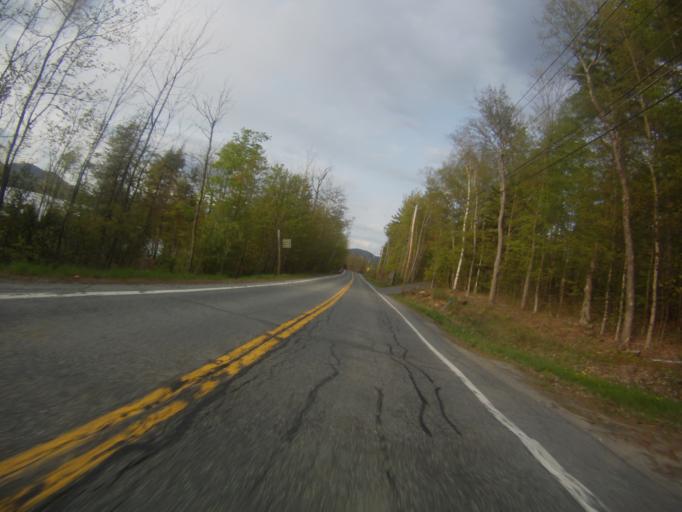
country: US
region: New York
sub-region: Warren County
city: Warrensburg
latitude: 43.7181
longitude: -73.6945
